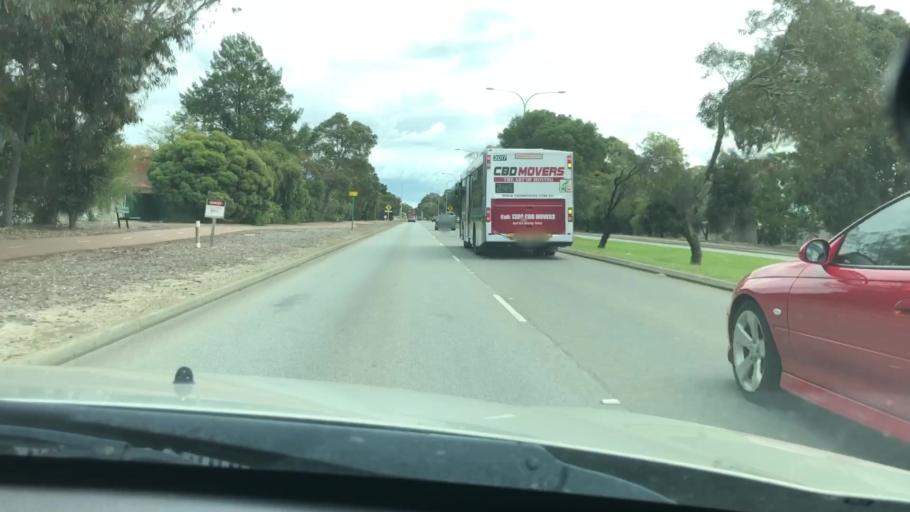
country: AU
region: Western Australia
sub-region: Armadale
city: Seville Grove
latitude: -32.1471
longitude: 115.9938
